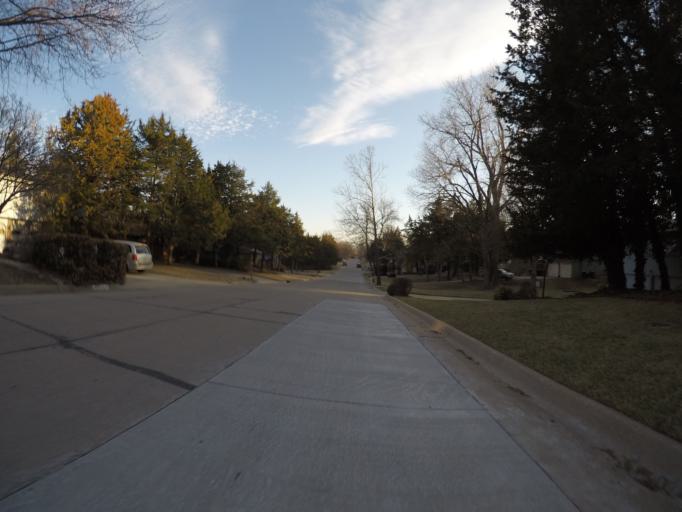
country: US
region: Kansas
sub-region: Riley County
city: Manhattan
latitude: 39.1999
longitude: -96.6243
